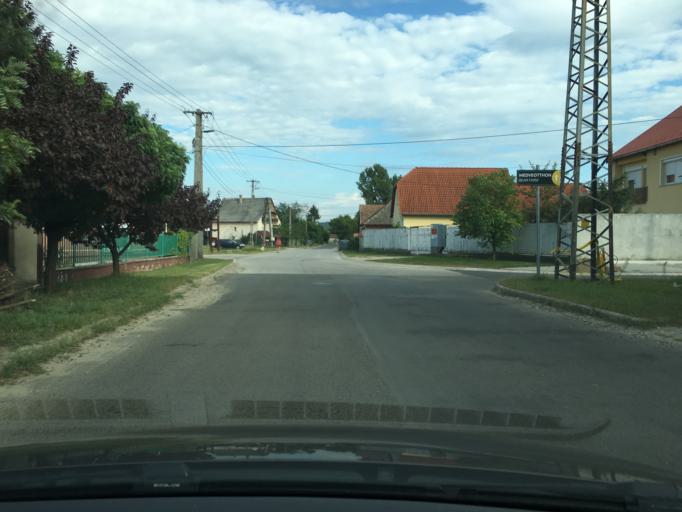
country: HU
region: Pest
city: Veresegyhaz
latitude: 47.6527
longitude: 19.2723
